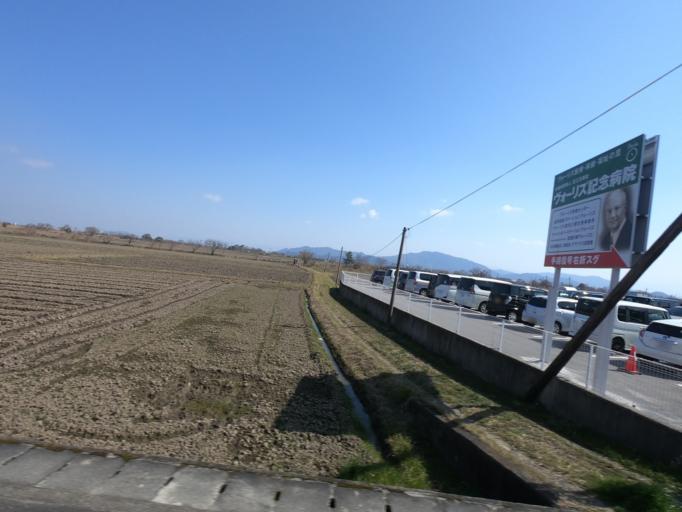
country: JP
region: Shiga Prefecture
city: Omihachiman
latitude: 35.1450
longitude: 136.0535
